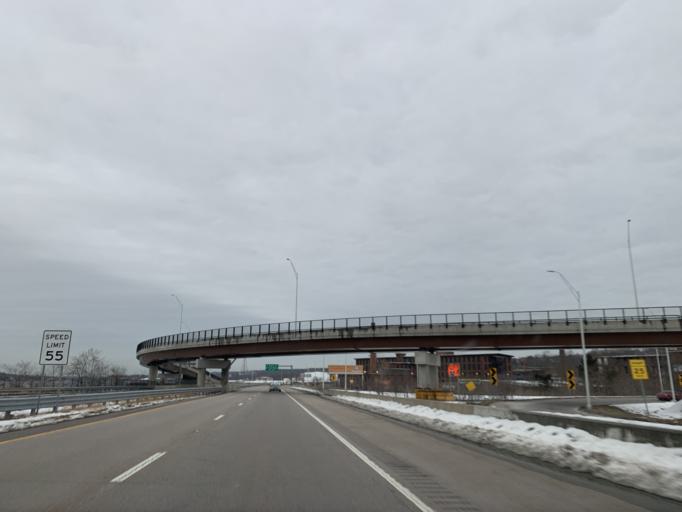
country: US
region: Massachusetts
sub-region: Bristol County
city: Fall River
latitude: 41.7261
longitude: -71.1487
